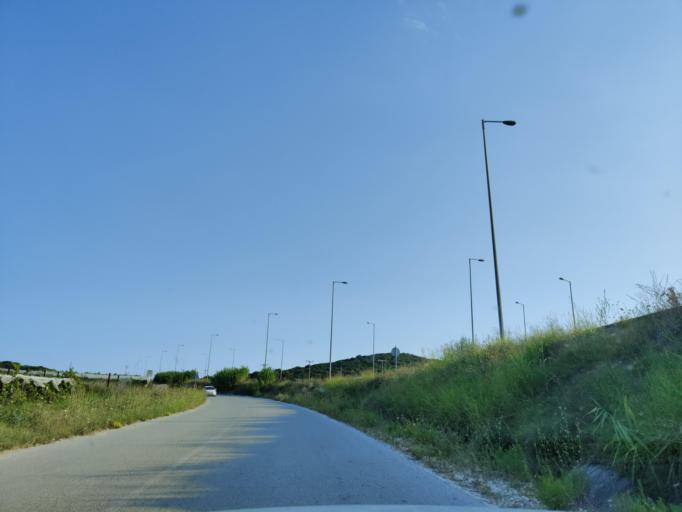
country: GR
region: East Macedonia and Thrace
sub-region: Nomos Kavalas
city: Nea Peramos
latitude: 40.8215
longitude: 24.2854
